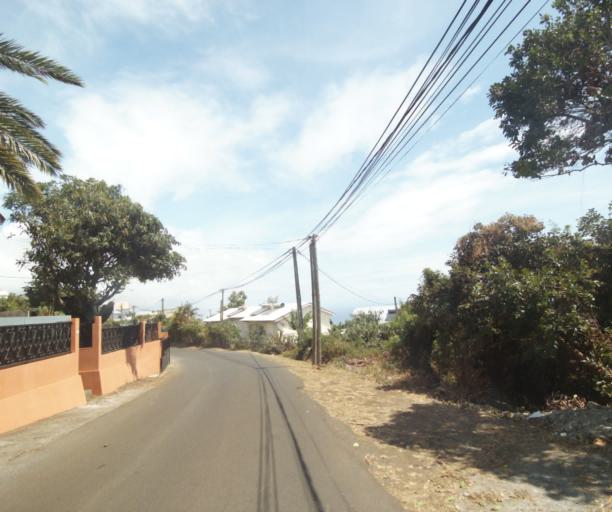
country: RE
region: Reunion
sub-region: Reunion
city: Trois-Bassins
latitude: -21.0987
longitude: 55.2774
